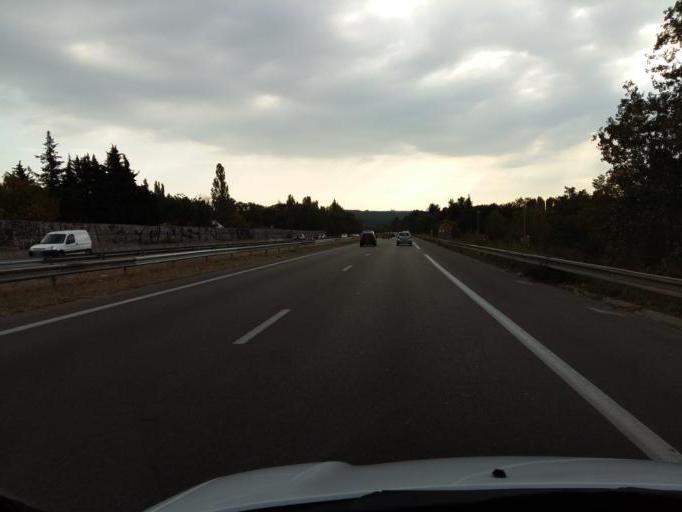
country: FR
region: Provence-Alpes-Cote d'Azur
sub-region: Departement des Bouches-du-Rhone
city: Bouc-Bel-Air
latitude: 43.4589
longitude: 5.4027
